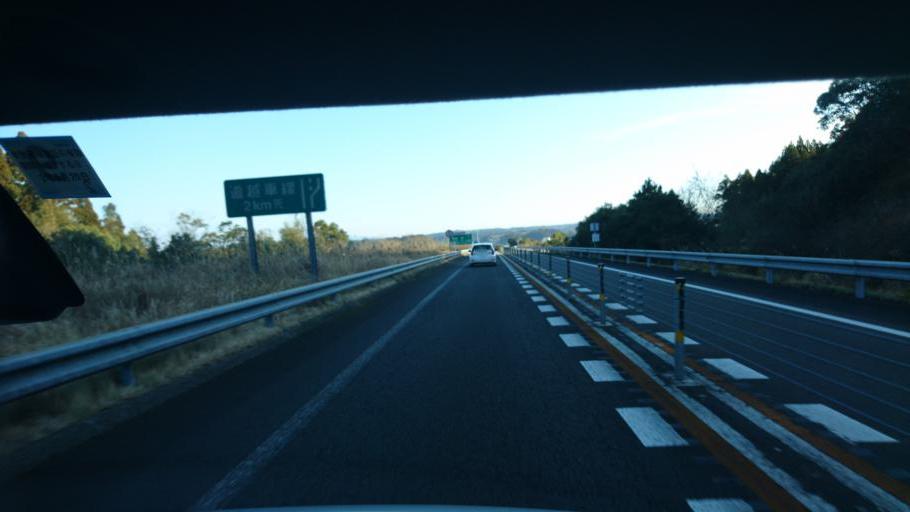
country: JP
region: Miyazaki
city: Miyazaki-shi
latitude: 31.9668
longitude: 131.3622
